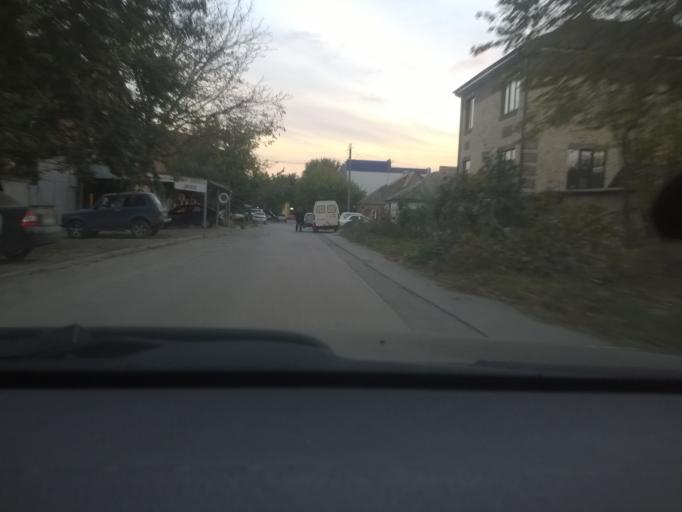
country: RU
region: Rostov
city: Rostov-na-Donu
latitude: 47.2134
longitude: 39.6493
